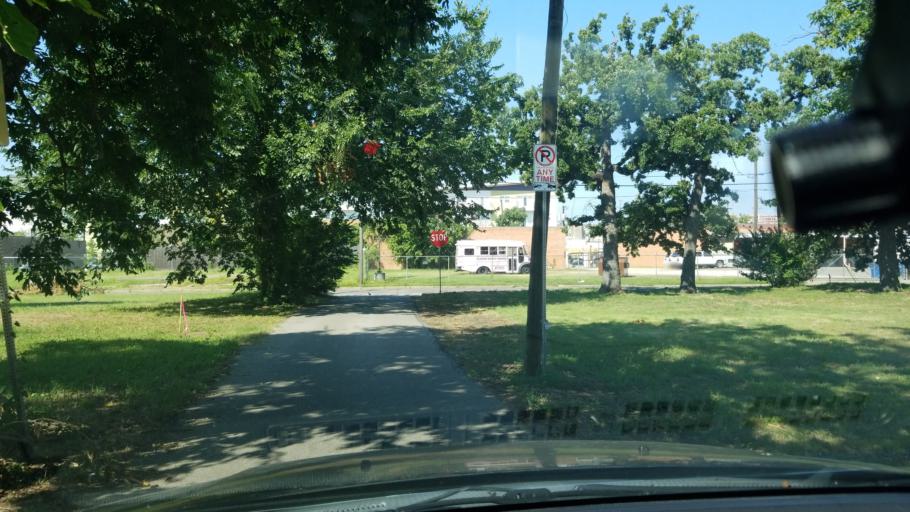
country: US
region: Texas
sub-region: Dallas County
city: Dallas
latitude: 32.7679
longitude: -96.7885
